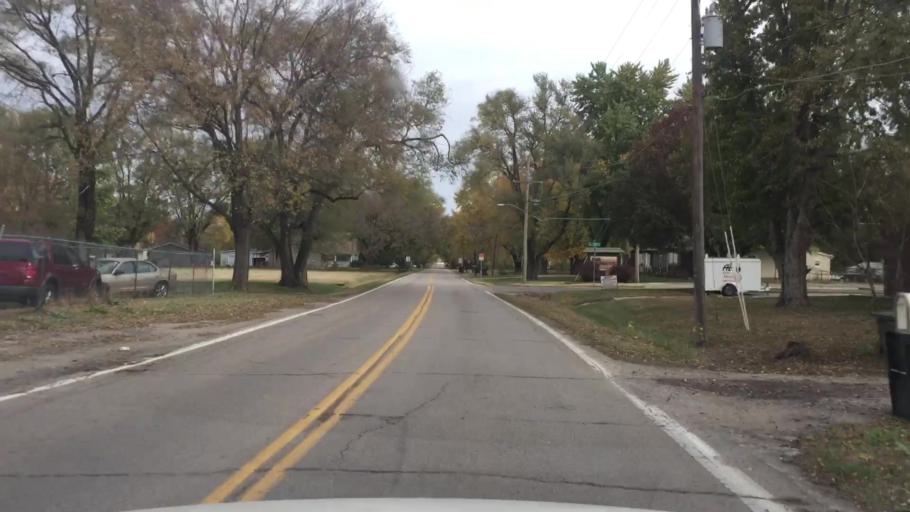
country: US
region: Kansas
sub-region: Shawnee County
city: Topeka
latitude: 39.0798
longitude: -95.6731
